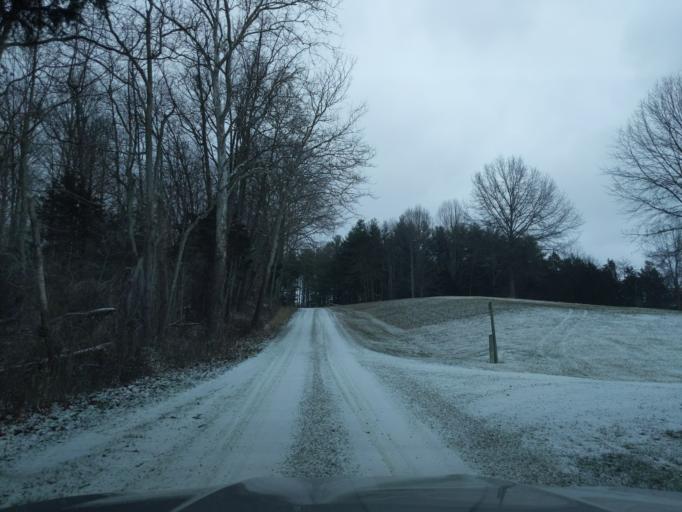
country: US
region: Indiana
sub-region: Decatur County
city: Westport
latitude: 39.2044
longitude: -85.4456
